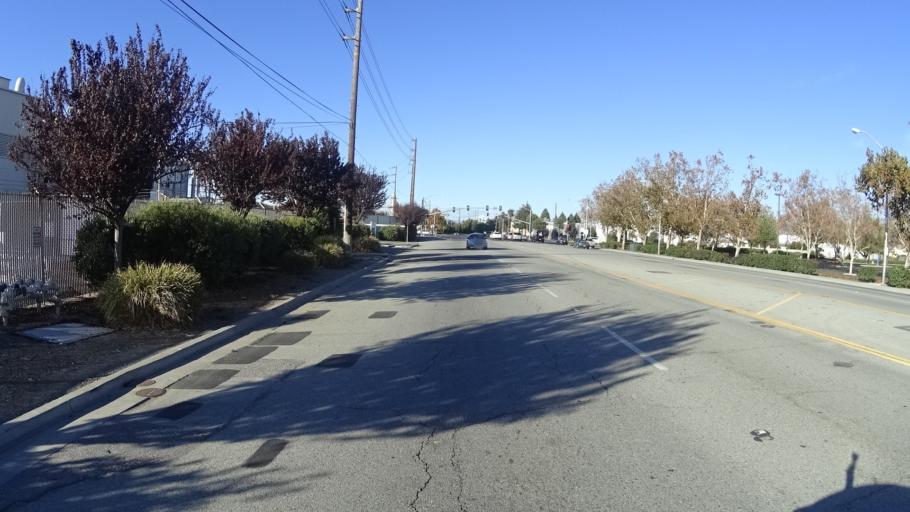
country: US
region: California
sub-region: Santa Clara County
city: Santa Clara
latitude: 37.3730
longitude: -121.9504
